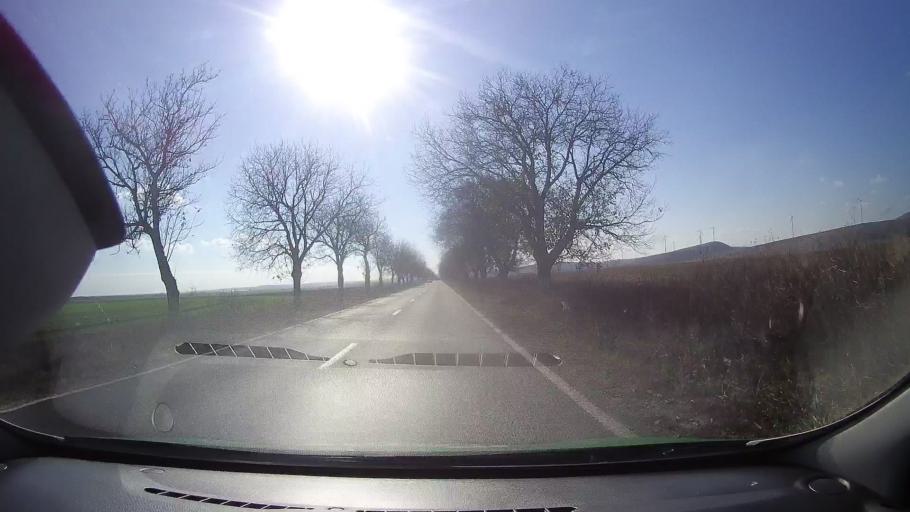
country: RO
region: Tulcea
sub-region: Comuna Ceamurlia de Jos
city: Ceamurlia de Jos
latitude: 44.7918
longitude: 28.6899
